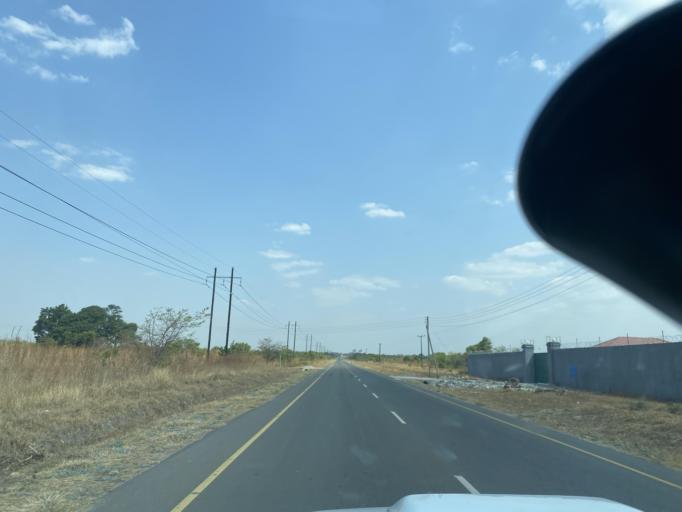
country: ZM
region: Lusaka
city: Lusaka
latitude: -15.3221
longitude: 28.0641
